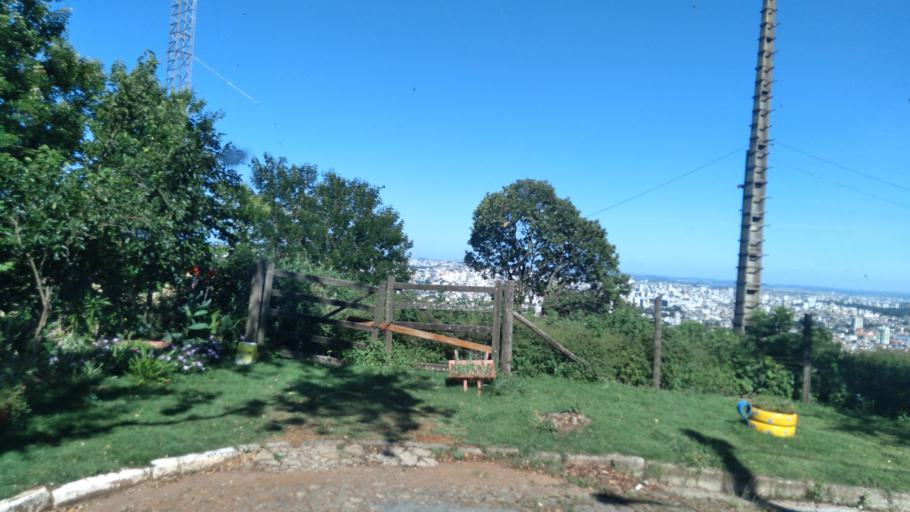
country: BR
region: Minas Gerais
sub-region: Belo Horizonte
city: Belo Horizonte
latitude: -19.9259
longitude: -43.8917
